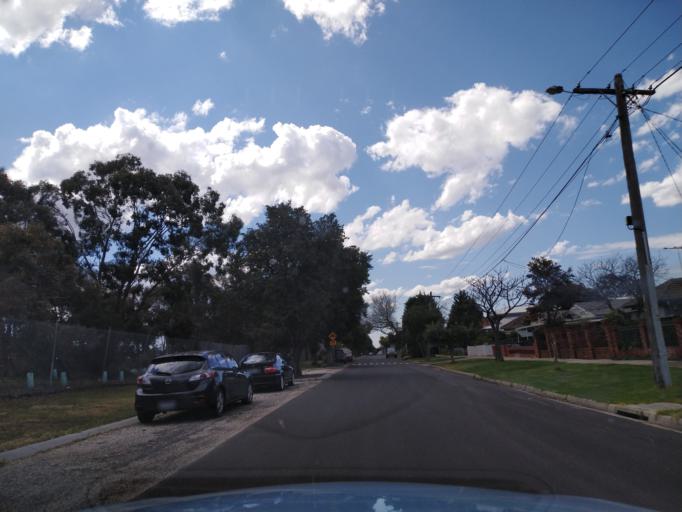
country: AU
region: Victoria
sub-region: Hobsons Bay
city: South Kingsville
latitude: -37.8382
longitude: 144.8754
